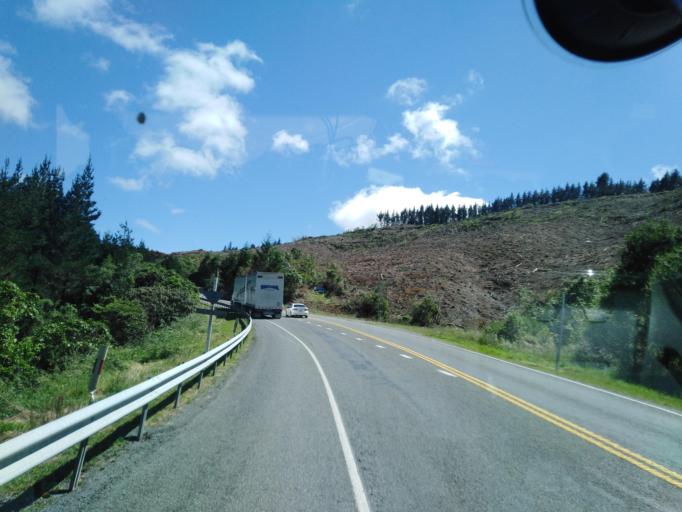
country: NZ
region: Nelson
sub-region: Nelson City
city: Nelson
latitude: -41.1946
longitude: 173.5580
